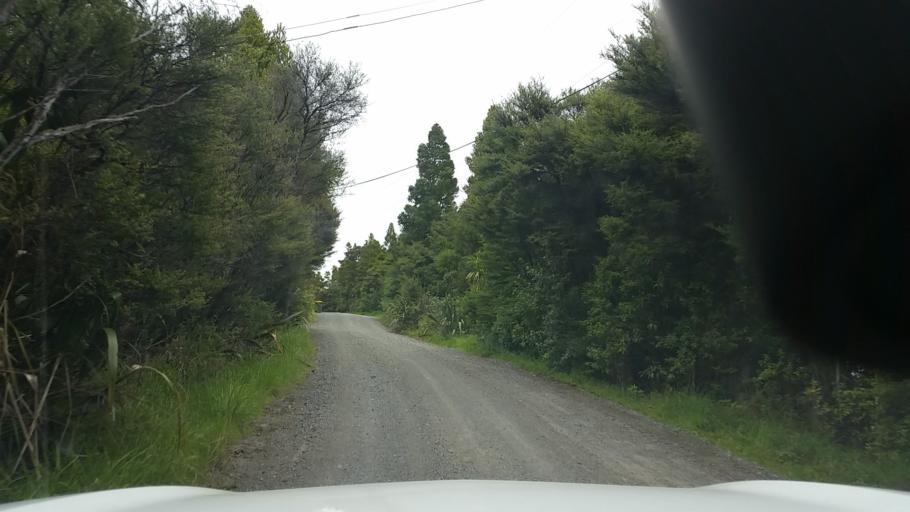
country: NZ
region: Auckland
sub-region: Auckland
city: Muriwai Beach
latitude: -36.8745
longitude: 174.4845
